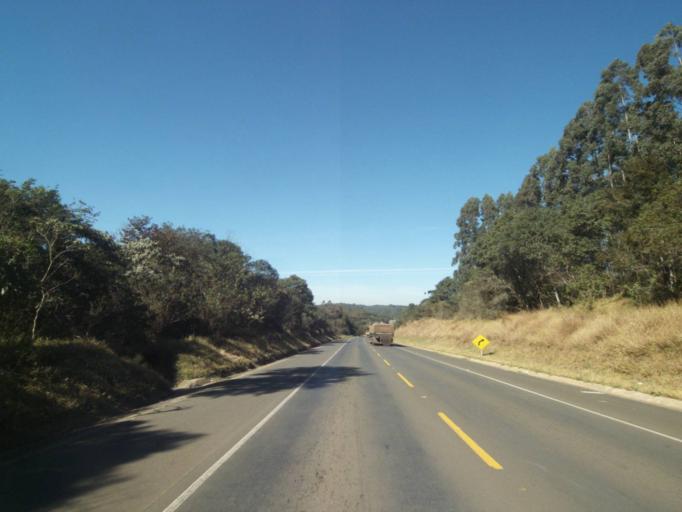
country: BR
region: Parana
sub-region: Tibagi
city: Tibagi
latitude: -24.5668
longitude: -50.4533
